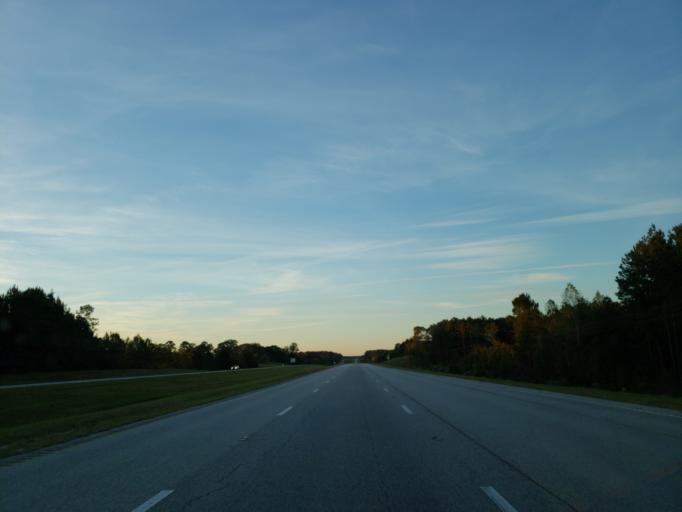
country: US
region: Mississippi
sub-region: Wayne County
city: Belmont
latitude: 31.4610
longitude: -88.4691
